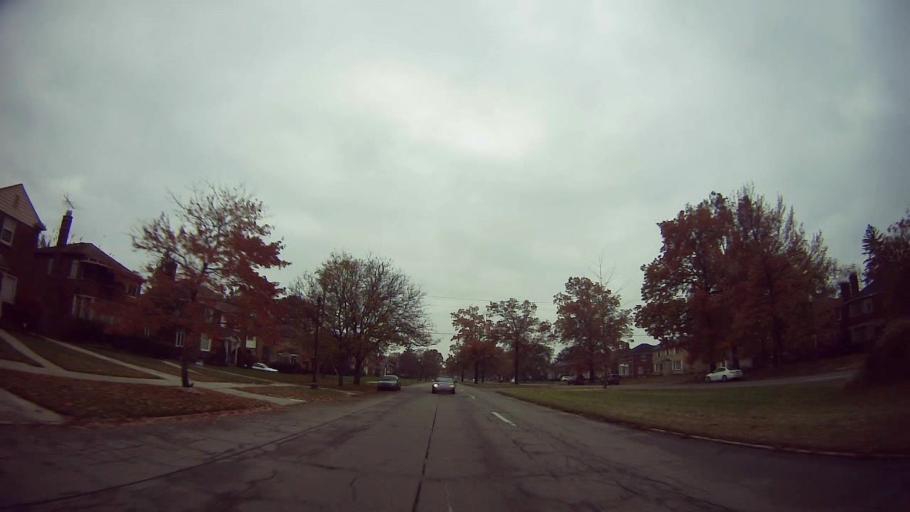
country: US
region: Michigan
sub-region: Oakland County
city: Oak Park
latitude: 42.4262
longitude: -83.1752
